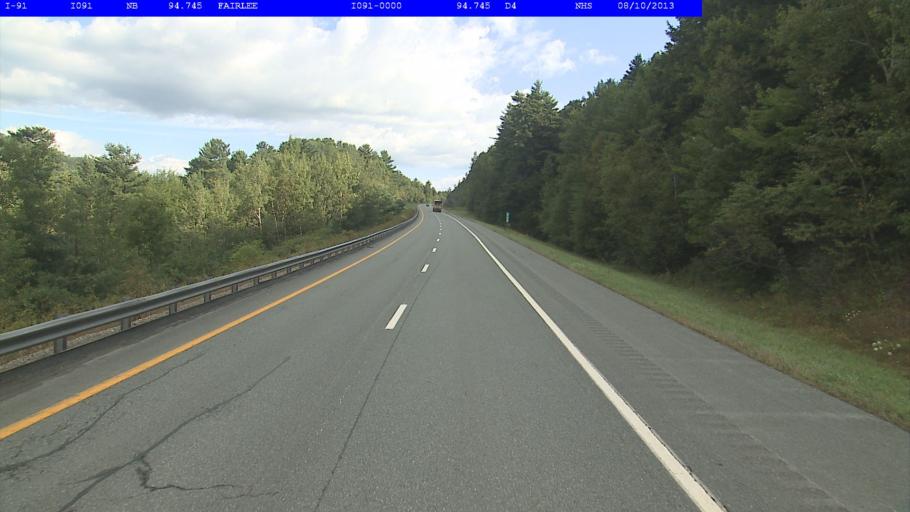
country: US
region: New Hampshire
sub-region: Grafton County
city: Orford
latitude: 43.9437
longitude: -72.1316
